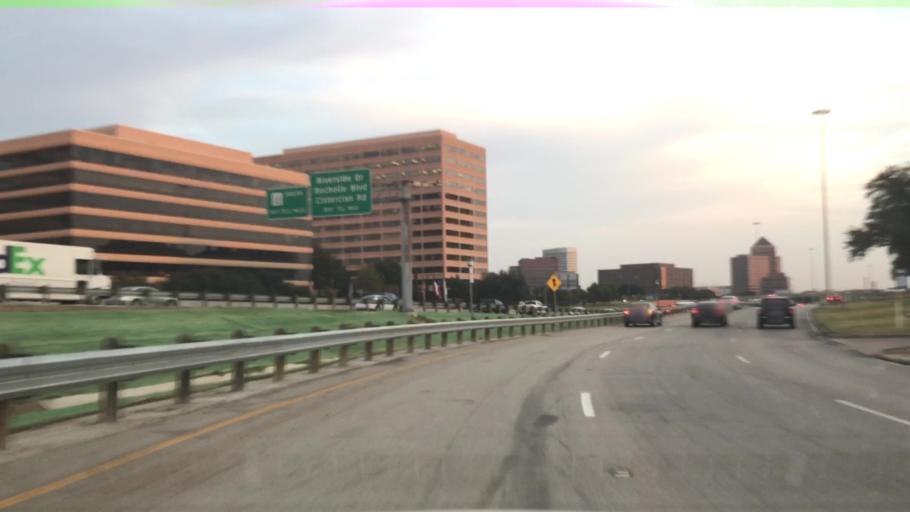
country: US
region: Texas
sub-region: Dallas County
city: Irving
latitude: 32.8666
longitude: -96.9429
